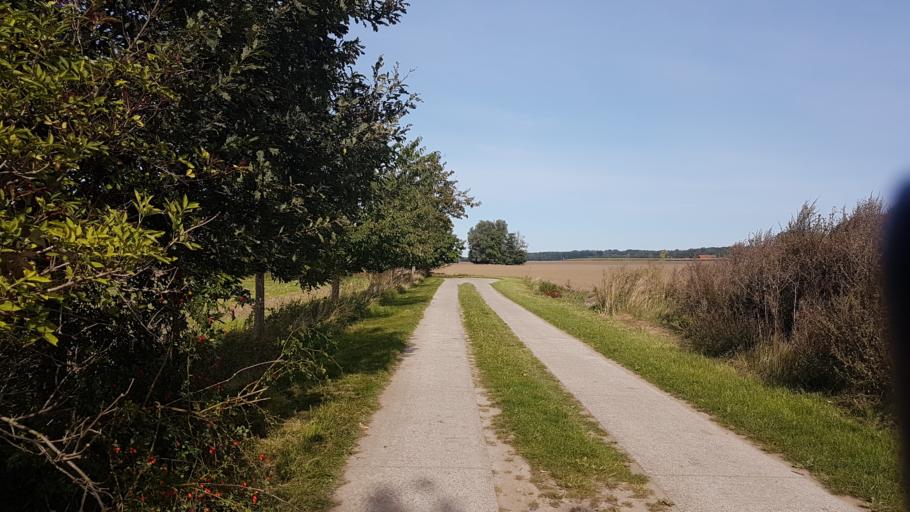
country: DE
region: Mecklenburg-Vorpommern
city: Gingst
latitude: 54.4118
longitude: 13.2578
